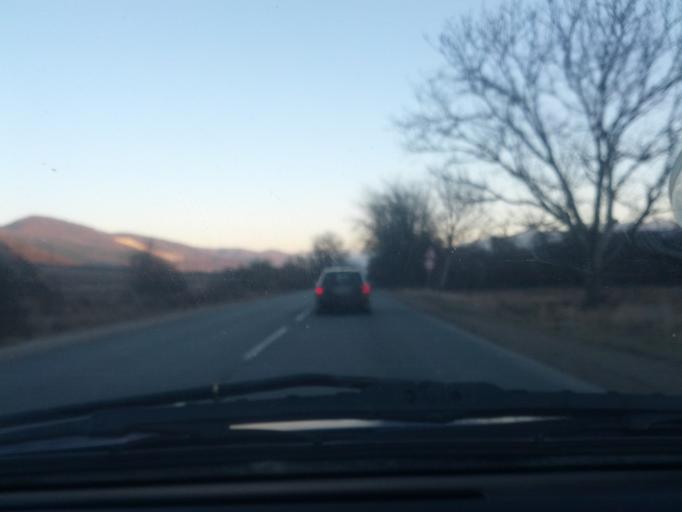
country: BG
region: Sofiya
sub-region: Obshtina Botevgrad
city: Botevgrad
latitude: 42.9894
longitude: 23.7256
